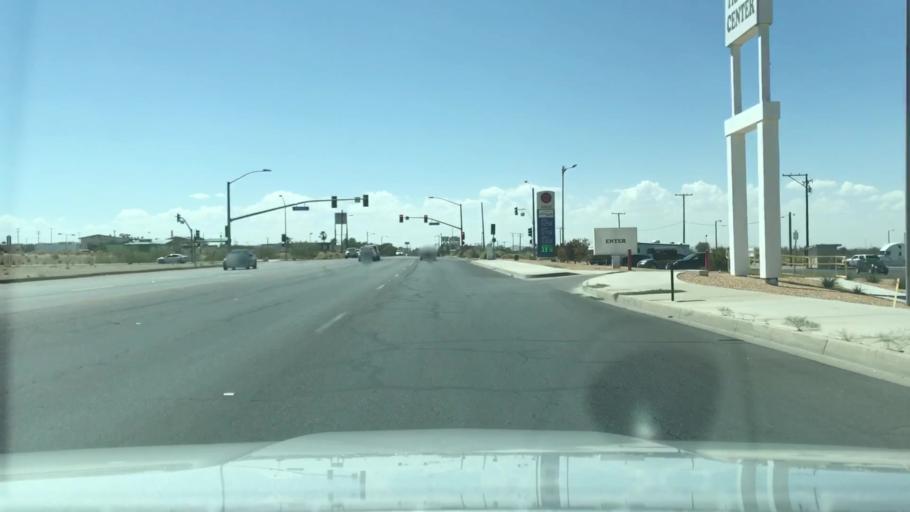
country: US
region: California
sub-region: San Bernardino County
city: Barstow Heights
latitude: 34.8919
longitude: -117.0563
